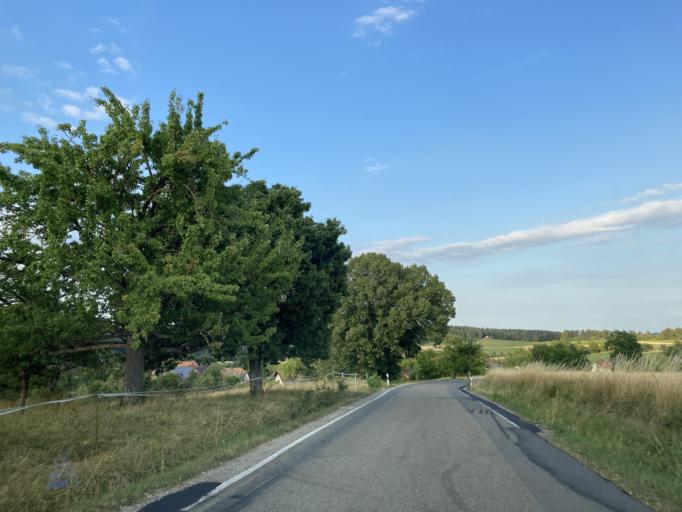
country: DE
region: Baden-Wuerttemberg
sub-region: Karlsruhe Region
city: Ebhausen
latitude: 48.6208
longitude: 8.6574
